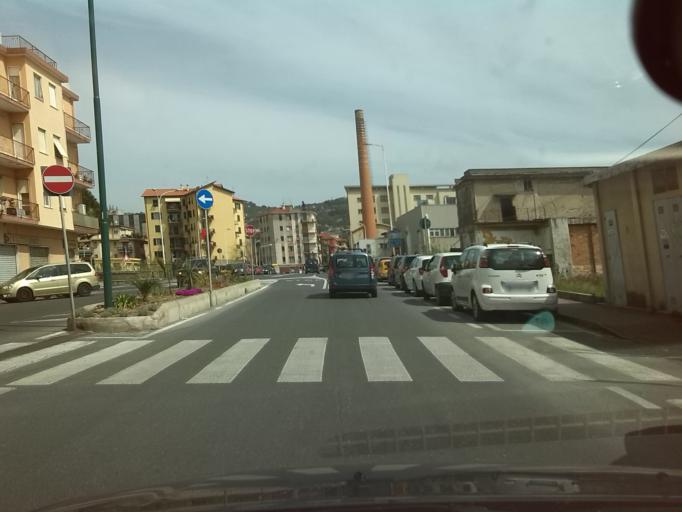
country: IT
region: Liguria
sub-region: Provincia di Imperia
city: Imperia
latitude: 43.8876
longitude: 8.0354
